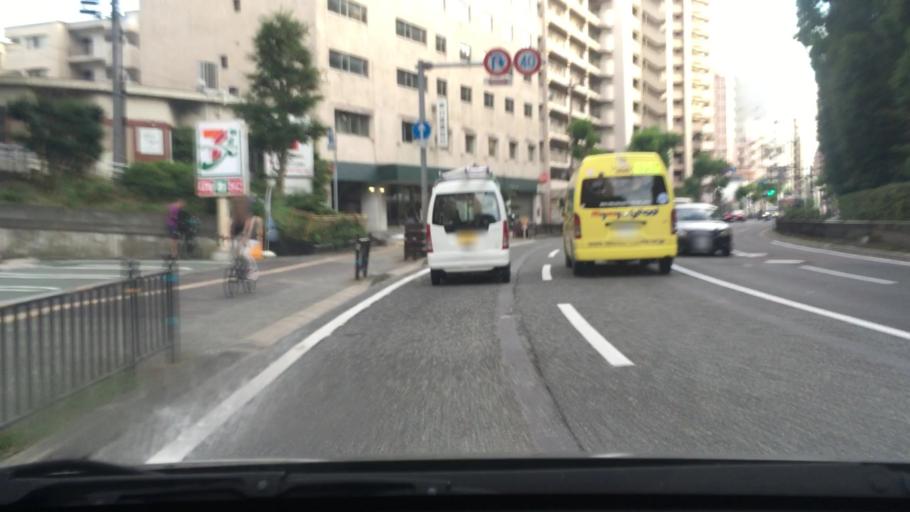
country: JP
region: Fukuoka
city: Fukuoka-shi
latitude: 33.5818
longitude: 130.3832
